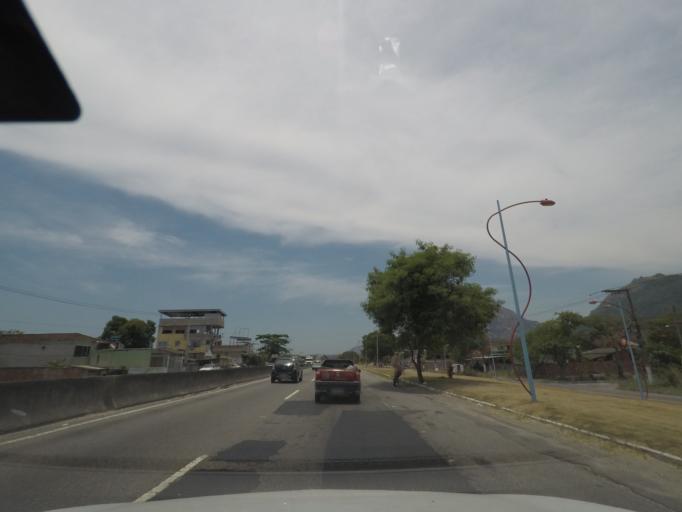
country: BR
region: Rio de Janeiro
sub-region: Marica
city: Marica
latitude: -22.9318
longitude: -42.8840
